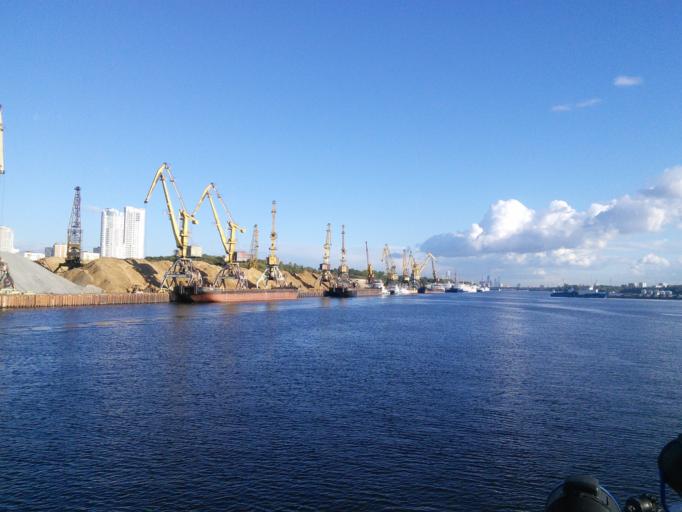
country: RU
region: Moskovskaya
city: Levoberezhnyy
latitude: 55.8649
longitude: 37.4551
